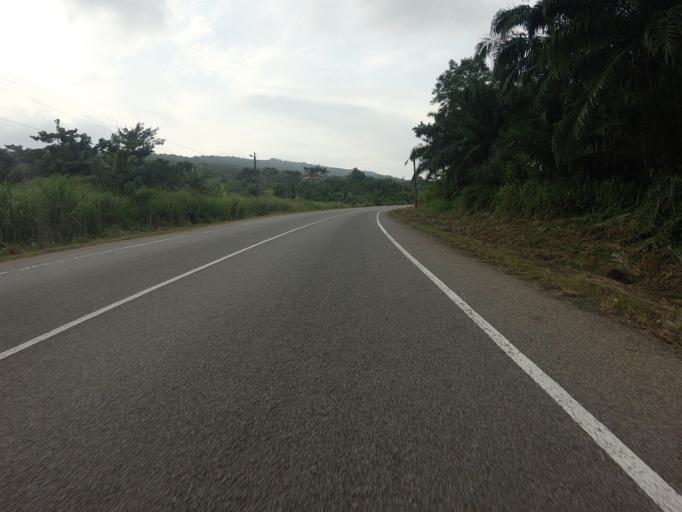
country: GH
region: Volta
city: Ho
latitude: 6.6514
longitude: 0.4696
